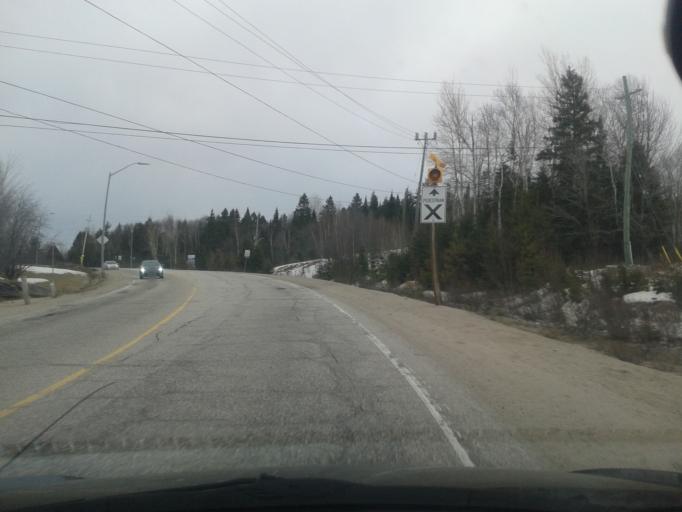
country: CA
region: Ontario
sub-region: Nipissing District
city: North Bay
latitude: 46.3411
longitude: -79.4887
